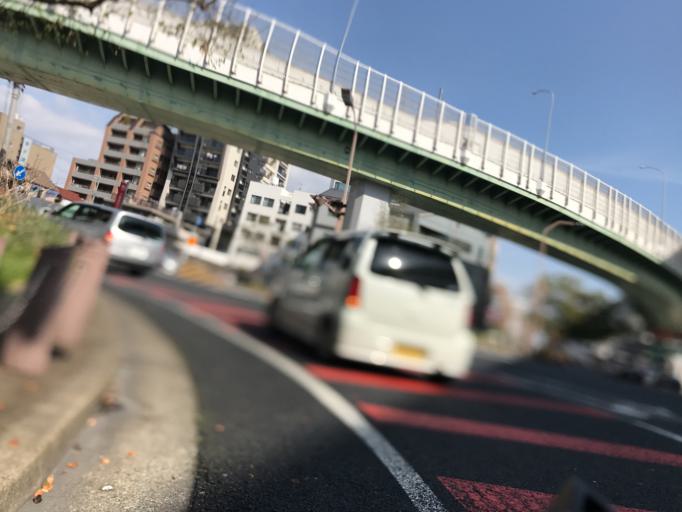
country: JP
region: Aichi
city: Nagoya-shi
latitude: 35.1783
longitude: 136.9138
